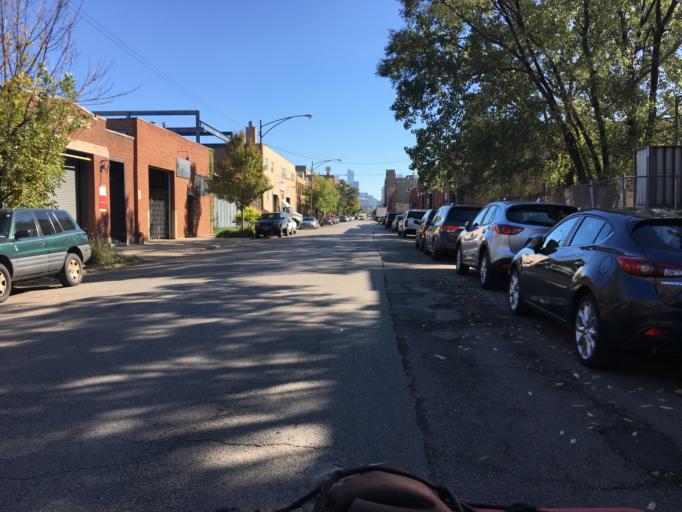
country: US
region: Illinois
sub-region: Cook County
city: Chicago
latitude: 41.8867
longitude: -87.6808
